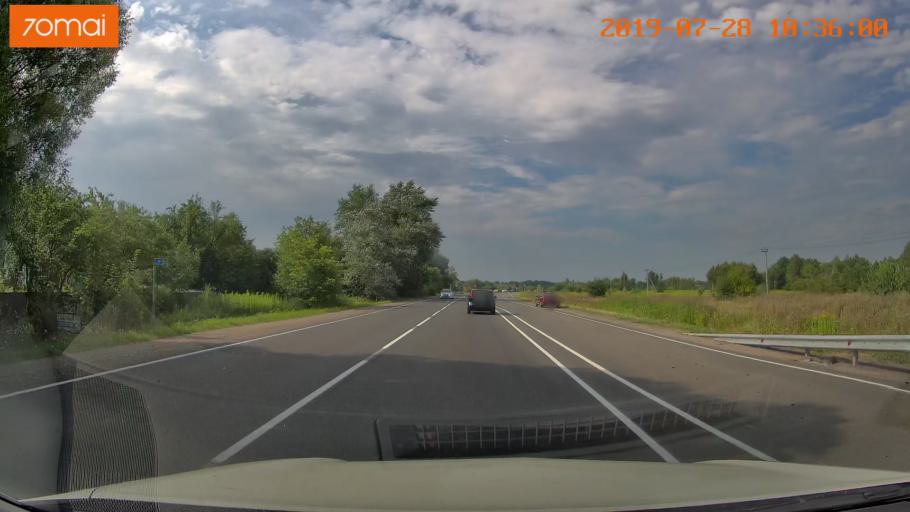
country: RU
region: Kaliningrad
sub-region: Gorod Kaliningrad
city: Kaliningrad
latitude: 54.7414
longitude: 20.4260
